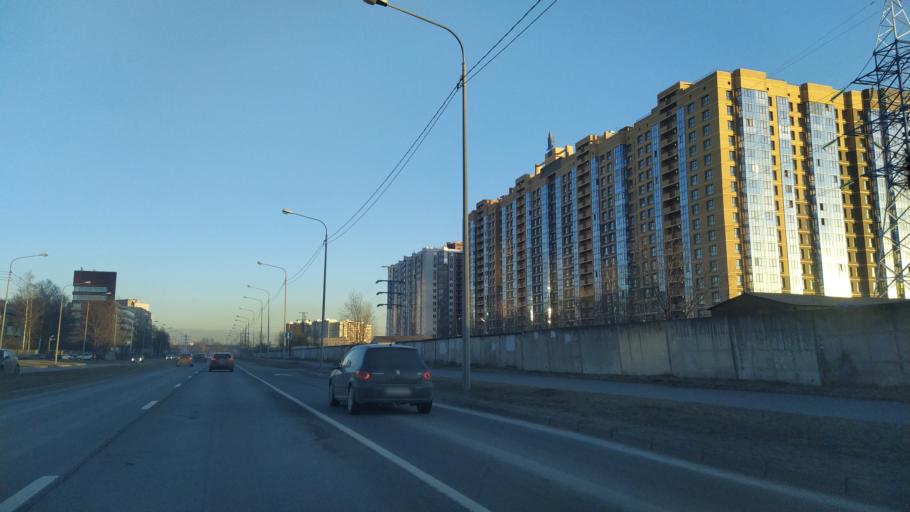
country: RU
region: St.-Petersburg
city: Kushelevka
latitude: 59.9826
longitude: 30.3726
